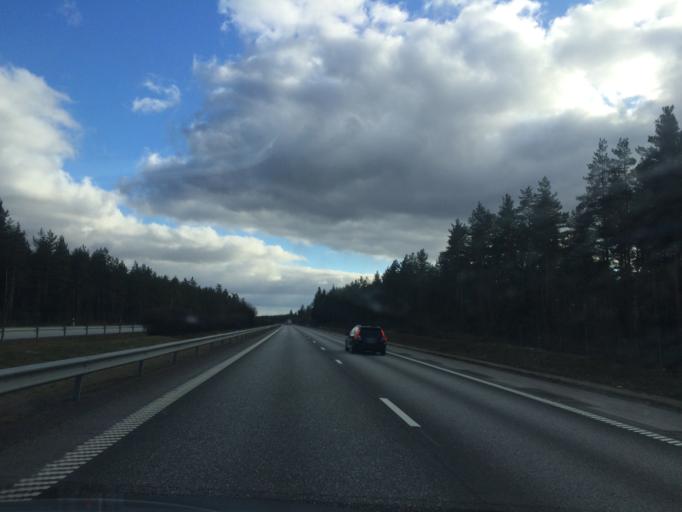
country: SE
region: Joenkoeping
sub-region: Vaggeryds Kommun
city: Skillingaryd
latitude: 57.3883
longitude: 14.0993
